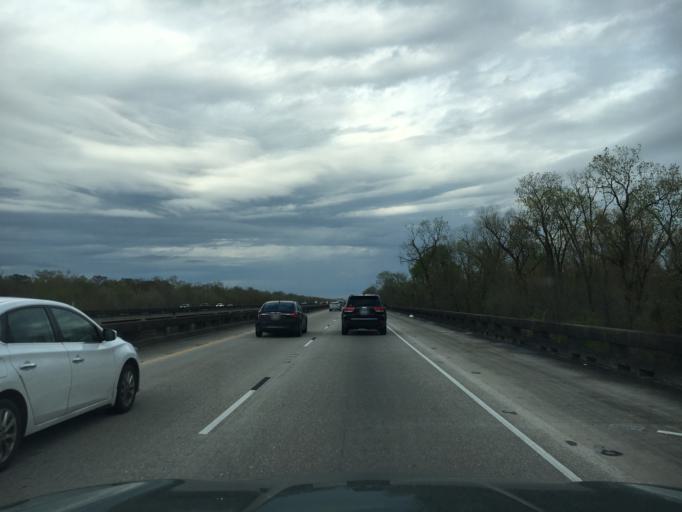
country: US
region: Louisiana
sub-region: Iberville Parish
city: Maringouin
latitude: 30.3730
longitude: -91.6090
